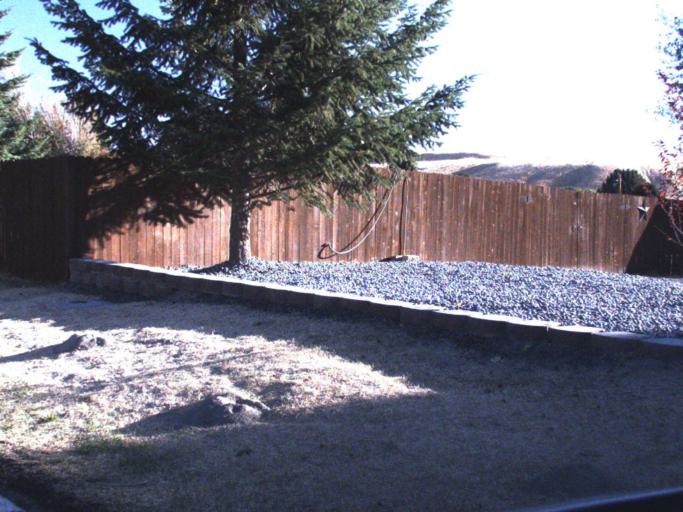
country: US
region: Washington
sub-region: Benton County
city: Benton City
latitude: 46.3135
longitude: -119.4932
